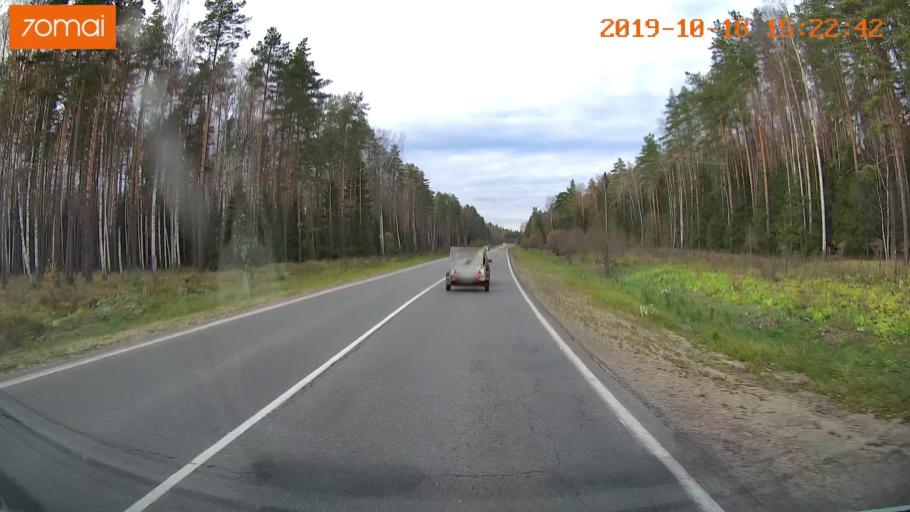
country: RU
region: Vladimir
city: Anopino
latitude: 55.7103
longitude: 40.7290
